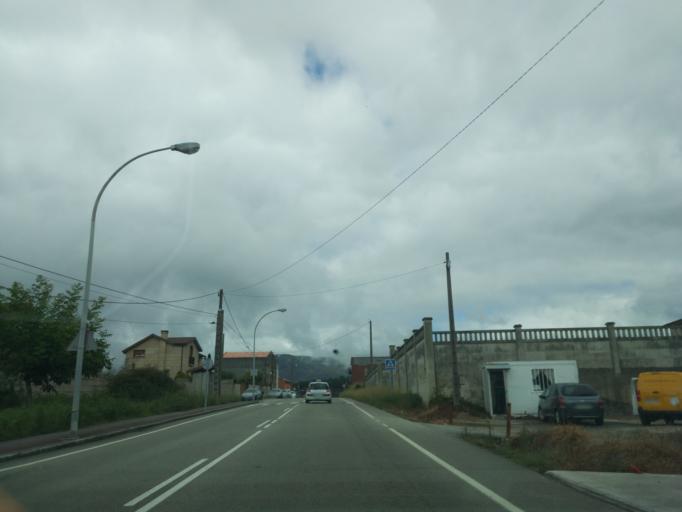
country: ES
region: Galicia
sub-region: Provincia da Coruna
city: Boiro
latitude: 42.6447
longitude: -8.8722
